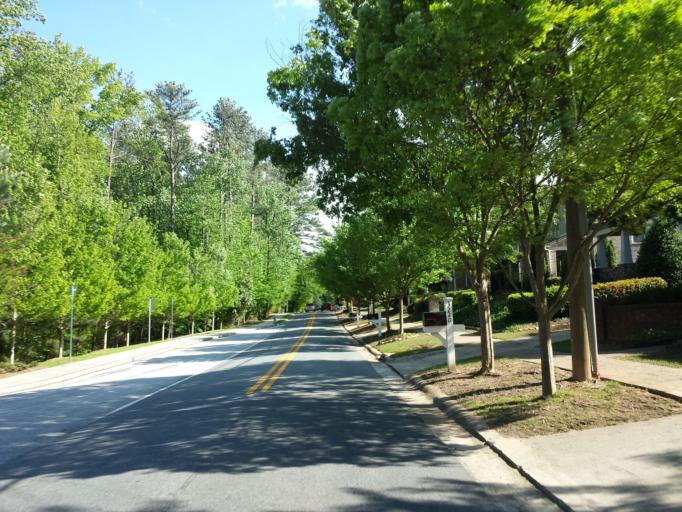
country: US
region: Georgia
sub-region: Cobb County
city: Smyrna
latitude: 33.8754
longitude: -84.5193
